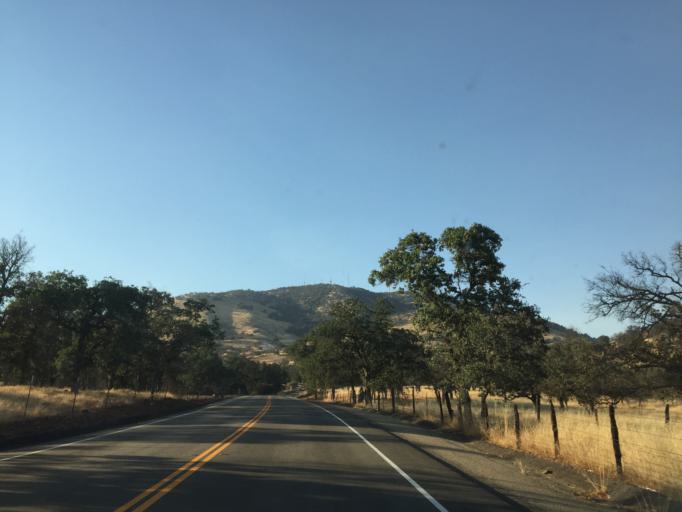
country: US
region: California
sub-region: Fresno County
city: Squaw Valley
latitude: 36.7253
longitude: -119.2853
